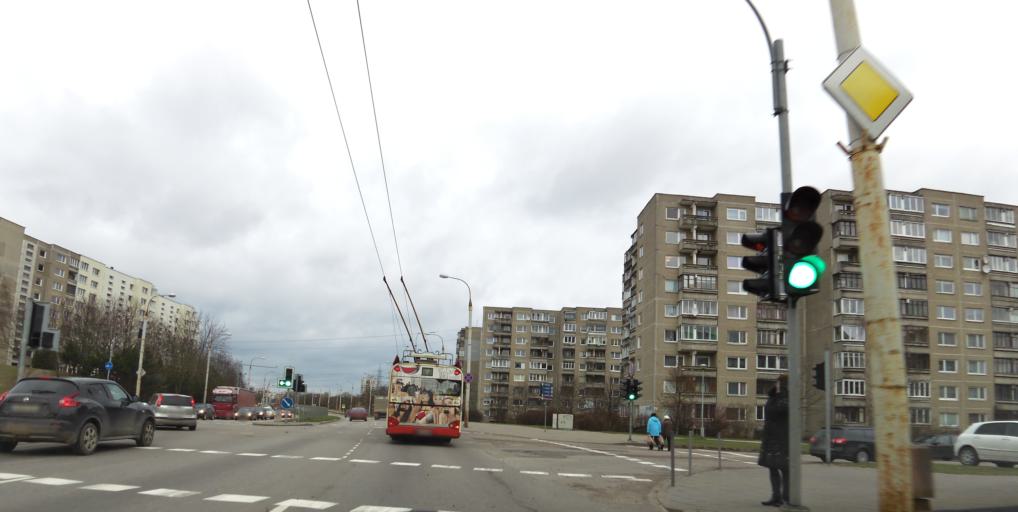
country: LT
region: Vilnius County
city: Justiniskes
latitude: 54.7209
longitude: 25.2229
